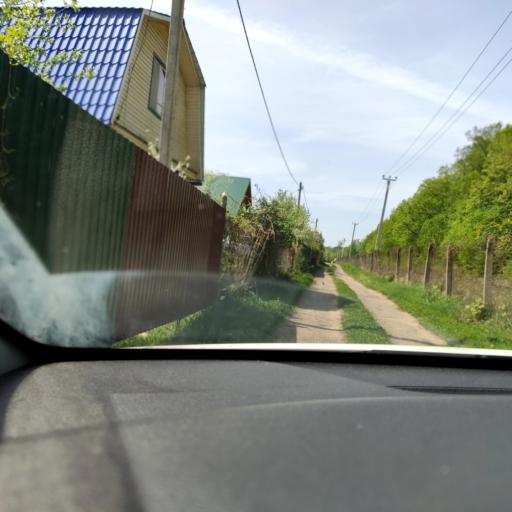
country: RU
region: Tatarstan
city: Osinovo
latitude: 55.7491
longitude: 48.8112
